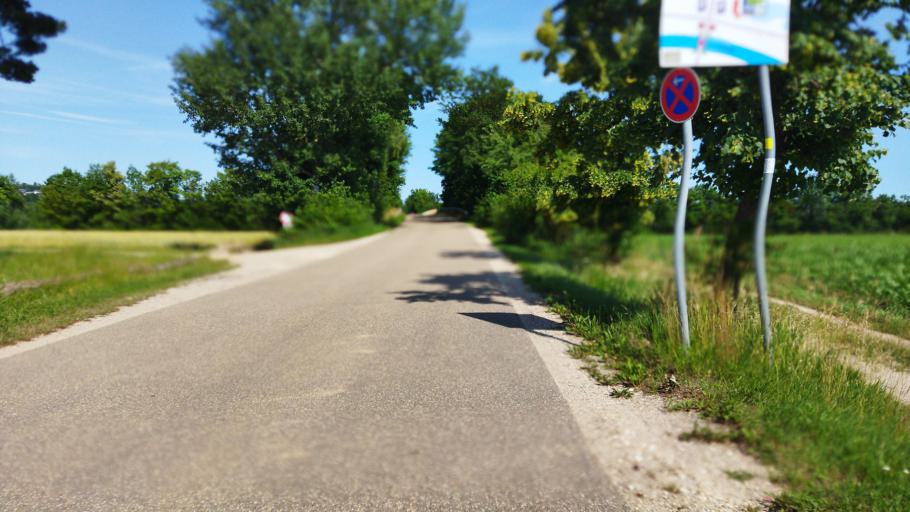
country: DE
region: Bavaria
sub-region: Lower Bavaria
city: Bad Abbach
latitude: 48.9364
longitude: 12.0237
